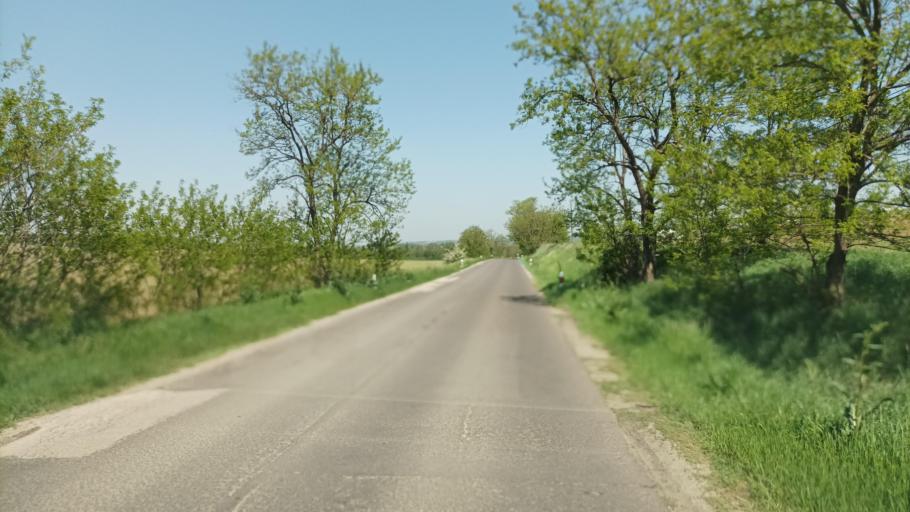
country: HU
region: Pest
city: Pecel
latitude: 47.4641
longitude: 19.3456
